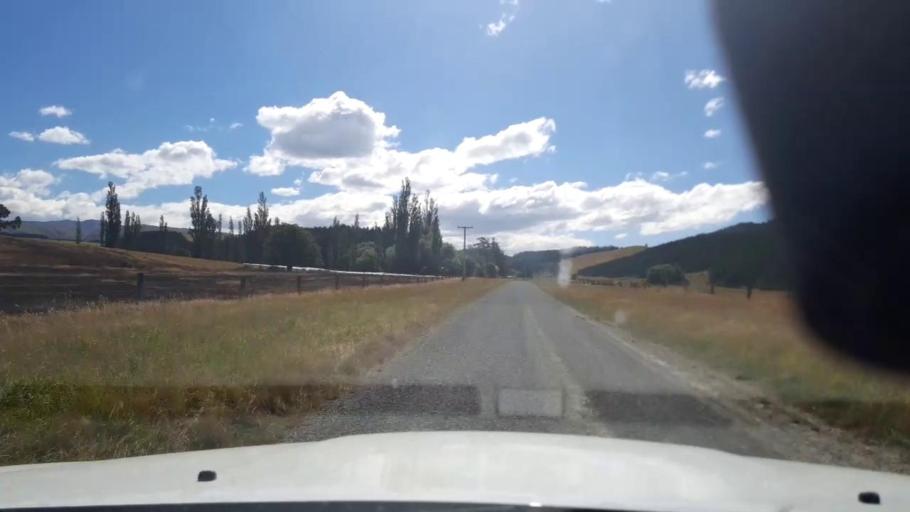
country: NZ
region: Canterbury
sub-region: Timaru District
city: Pleasant Point
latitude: -44.3141
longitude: 170.9242
